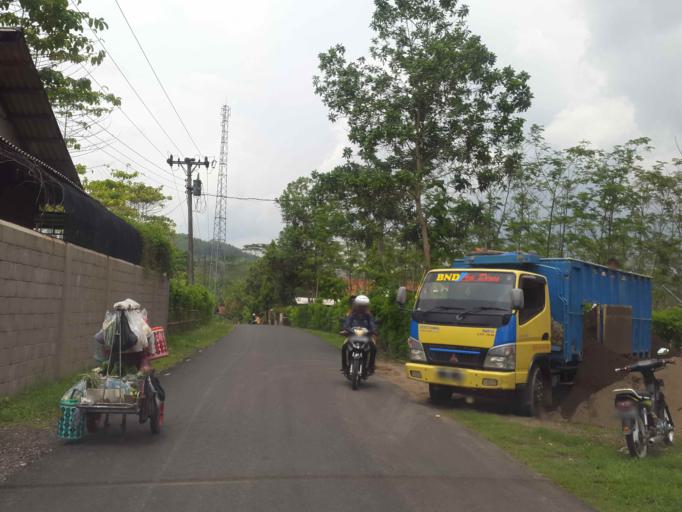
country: ID
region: Central Java
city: Pasanggrahan
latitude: -7.3902
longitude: 108.8861
